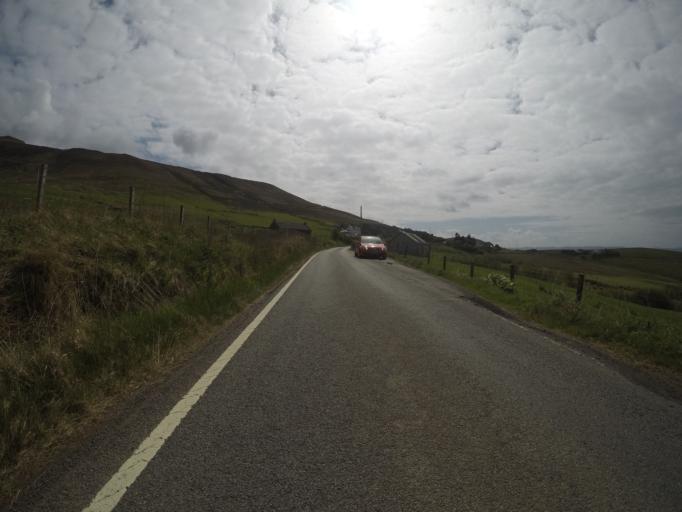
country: GB
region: Scotland
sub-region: Highland
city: Portree
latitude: 57.6138
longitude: -6.3709
